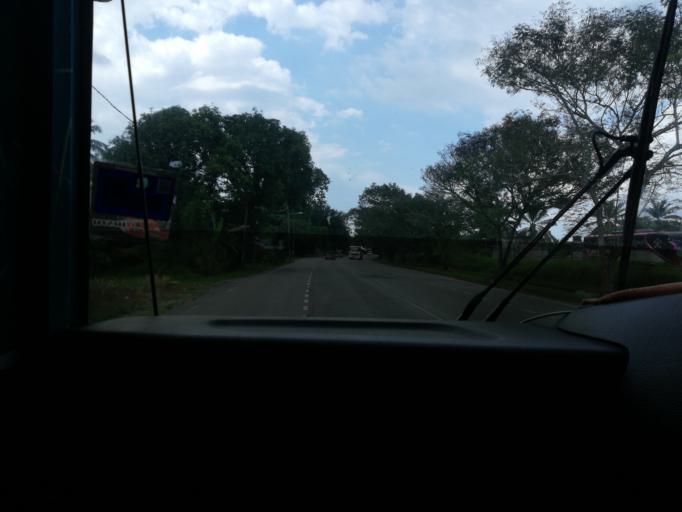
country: MY
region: Kedah
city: Kulim
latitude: 5.3655
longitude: 100.5810
